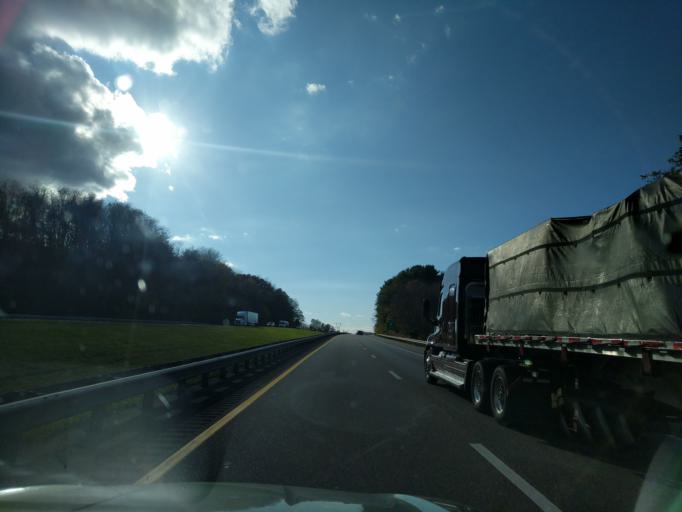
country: US
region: Virginia
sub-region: Smyth County
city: Atkins
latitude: 36.8659
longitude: -81.4183
